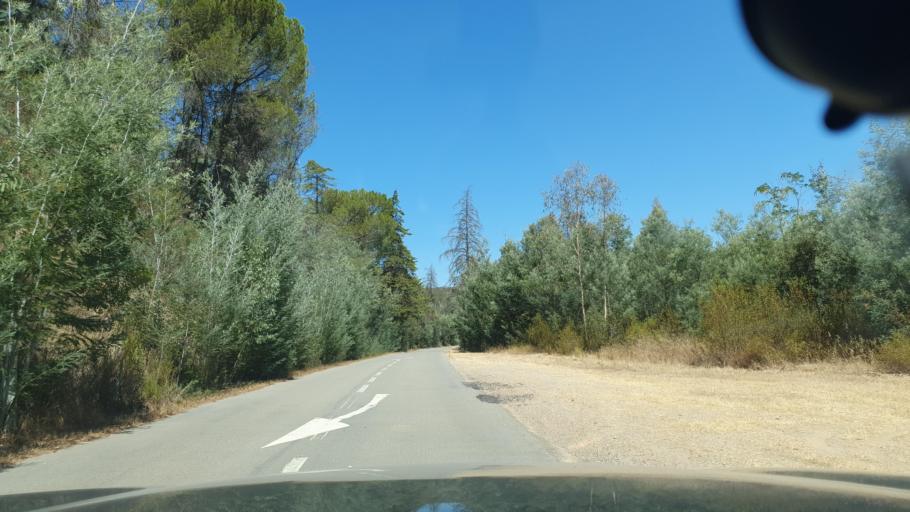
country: PT
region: Beja
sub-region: Odemira
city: Odemira
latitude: 37.5073
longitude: -8.4600
